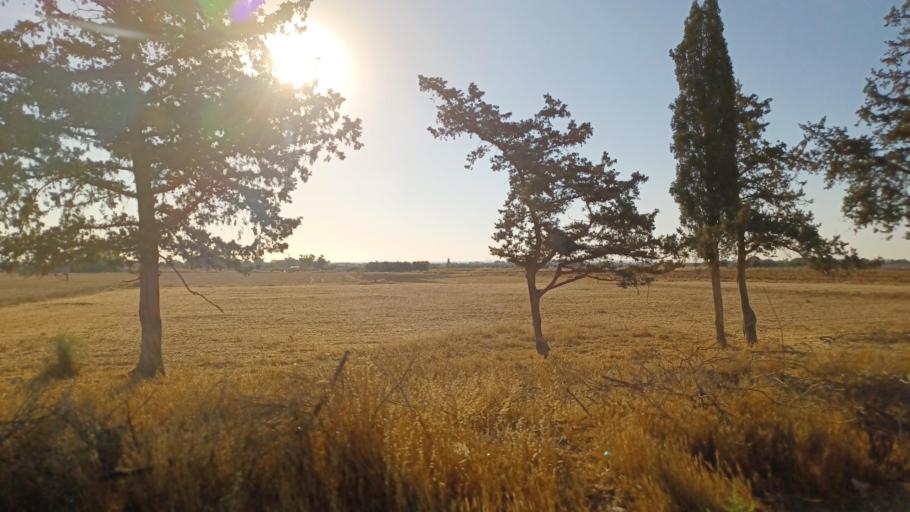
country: CY
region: Ammochostos
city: Achna
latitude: 35.0387
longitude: 33.7916
